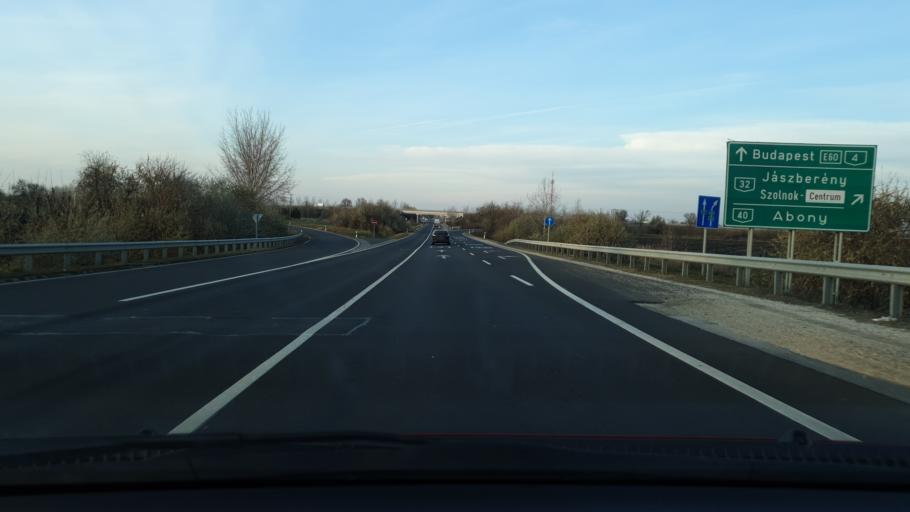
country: HU
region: Jasz-Nagykun-Szolnok
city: Toszeg
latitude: 47.1789
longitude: 20.1004
